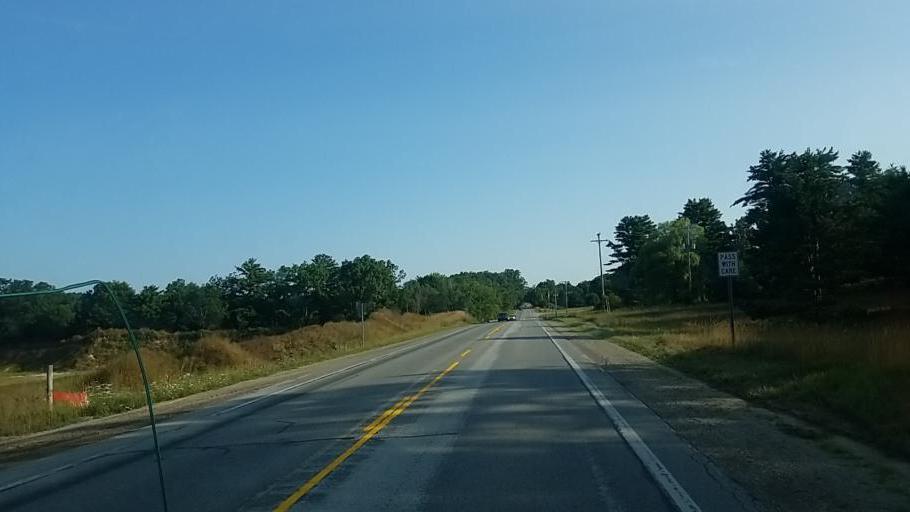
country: US
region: Michigan
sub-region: Newaygo County
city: Fremont
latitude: 43.4797
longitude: -86.0395
